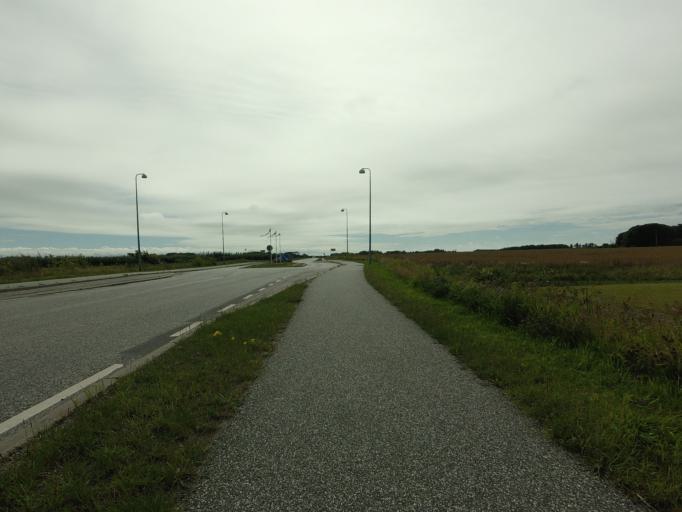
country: DK
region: North Denmark
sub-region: Hjorring Kommune
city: Vra
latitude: 57.3912
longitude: 9.7762
